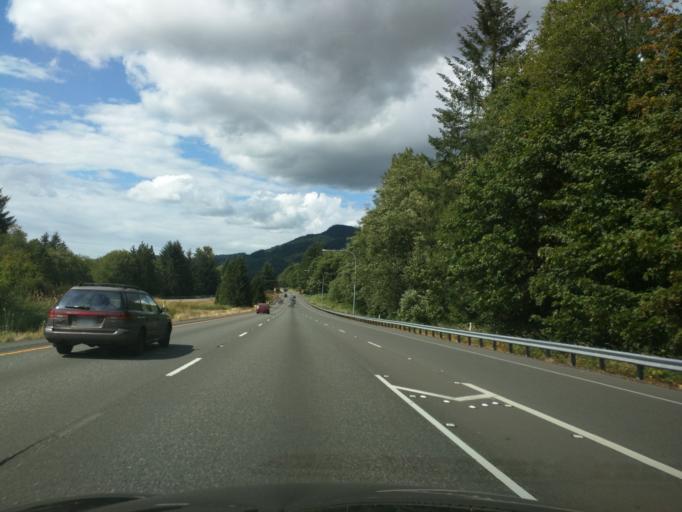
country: US
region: Washington
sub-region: Whatcom County
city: Sudden Valley
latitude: 48.6516
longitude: -122.3669
